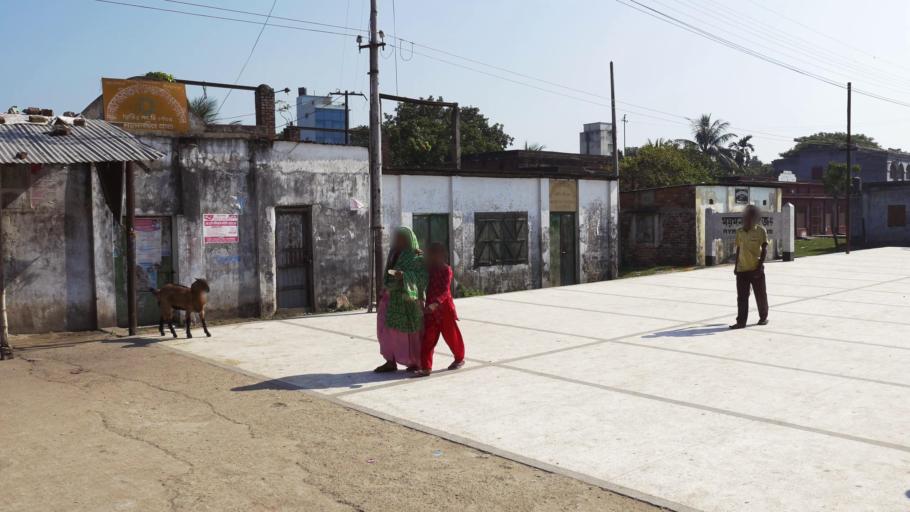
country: BD
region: Dhaka
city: Mymensingh
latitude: 24.6590
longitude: 90.4542
